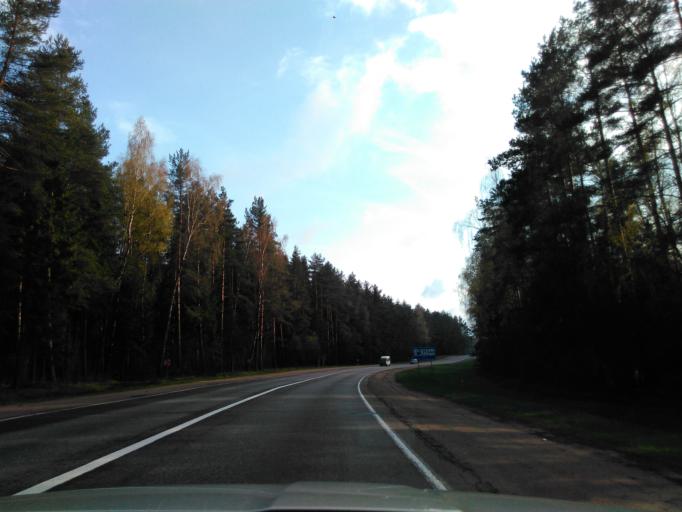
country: BY
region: Minsk
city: Lahoysk
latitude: 54.2490
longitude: 27.8494
